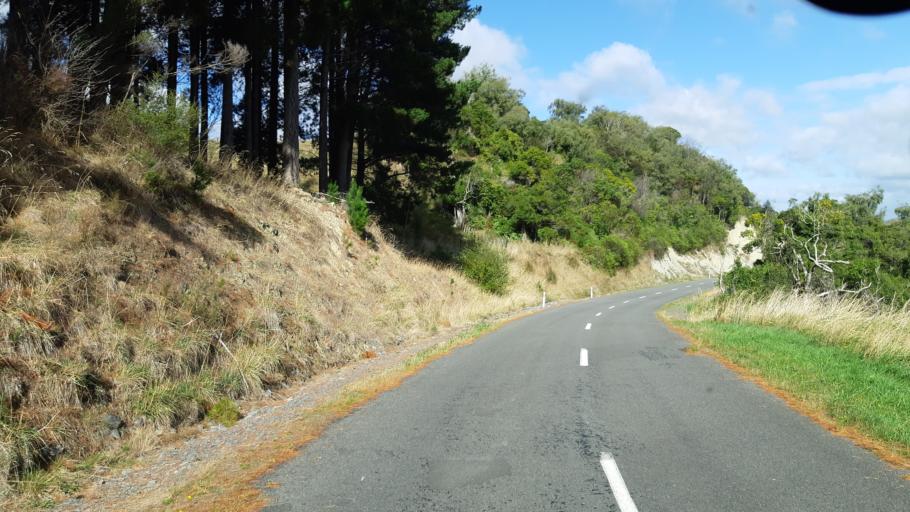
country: NZ
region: Manawatu-Wanganui
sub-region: Ruapehu District
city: Waiouru
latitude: -39.7457
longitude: 175.6652
